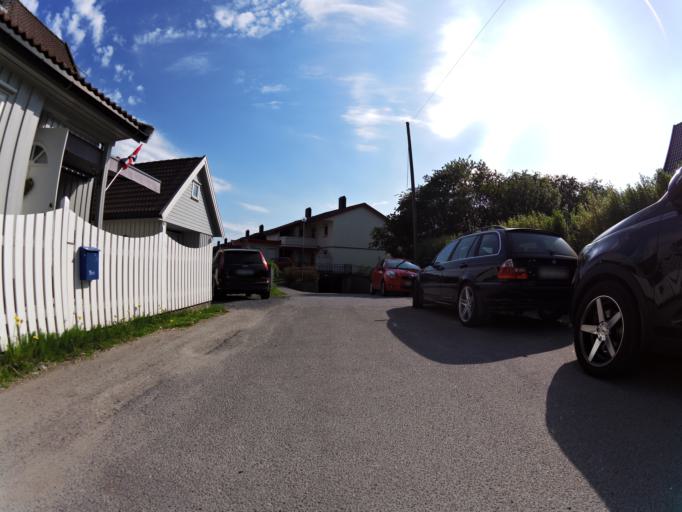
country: NO
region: Ostfold
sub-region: Fredrikstad
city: Fredrikstad
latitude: 59.2333
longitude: 10.9688
